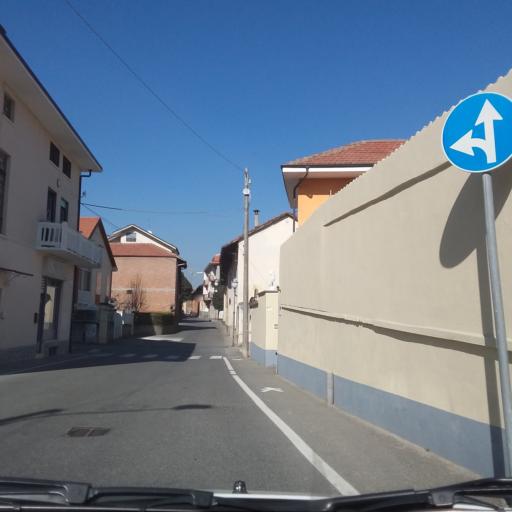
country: IT
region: Piedmont
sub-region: Provincia di Torino
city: Rivoli
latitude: 45.0639
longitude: 7.5166
